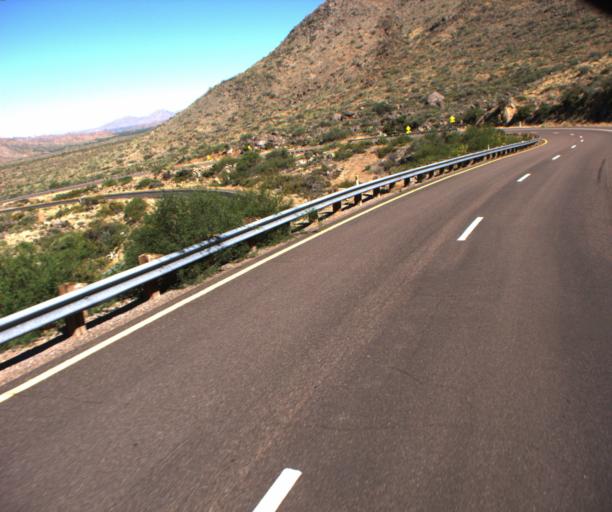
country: US
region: Arizona
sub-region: Yavapai County
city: Congress
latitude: 34.2068
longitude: -112.7983
